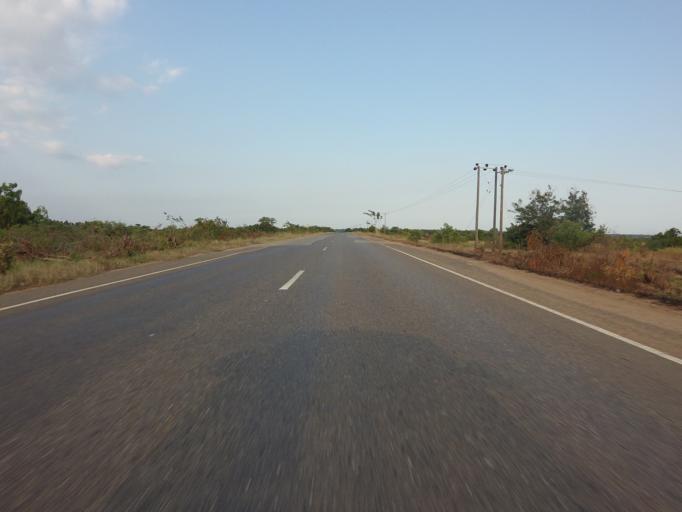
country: GH
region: Volta
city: Anloga
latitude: 6.0803
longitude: 0.5787
